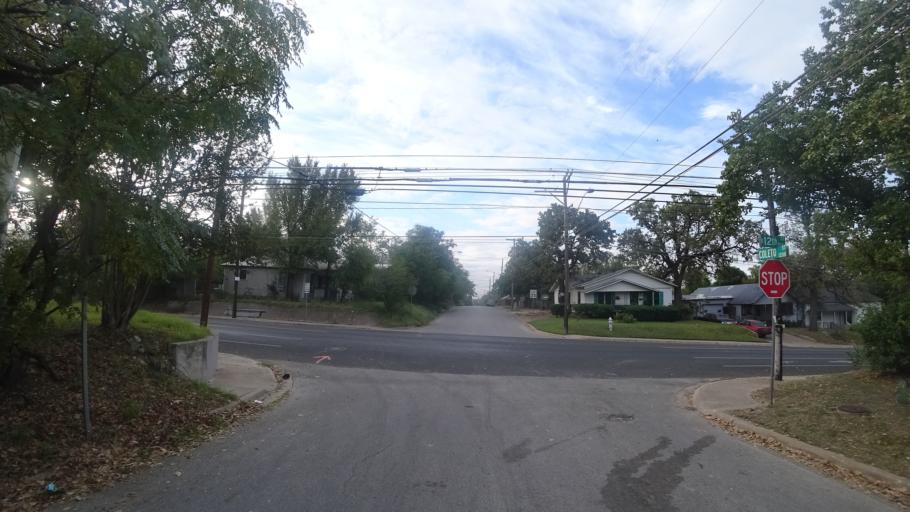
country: US
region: Texas
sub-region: Travis County
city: Austin
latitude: 30.2744
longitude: -97.7170
